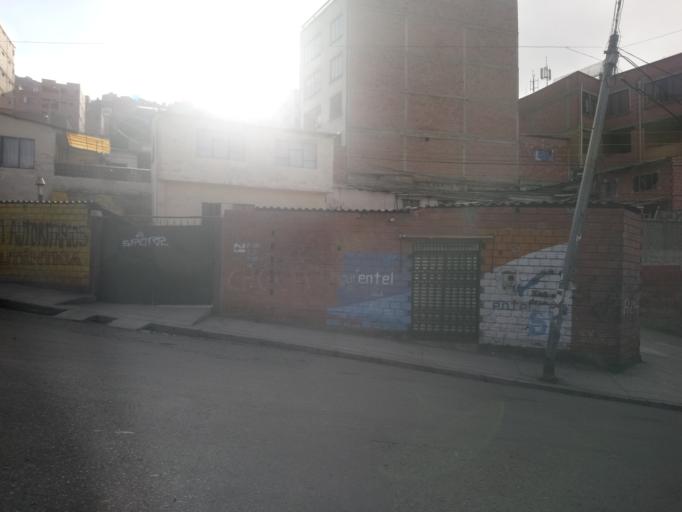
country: BO
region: La Paz
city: La Paz
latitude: -16.4959
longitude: -68.1113
